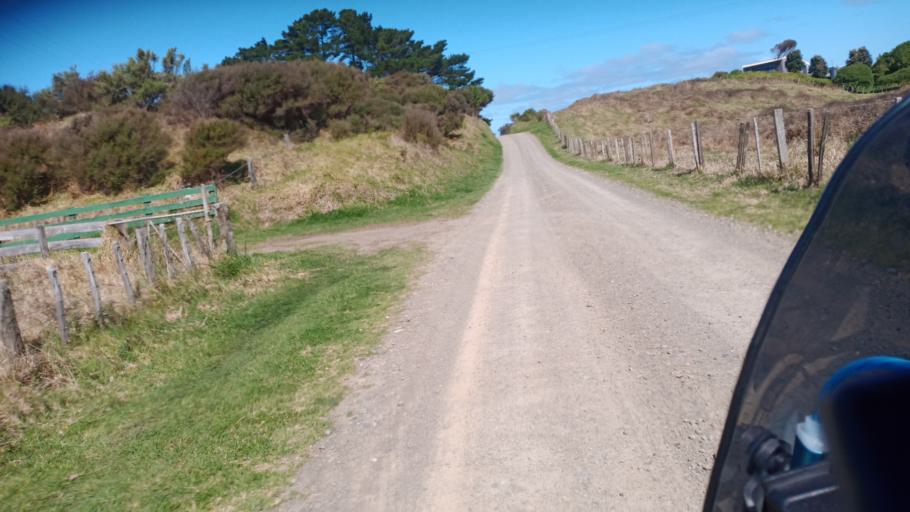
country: NZ
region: Gisborne
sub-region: Gisborne District
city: Gisborne
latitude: -39.0105
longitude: 177.8865
